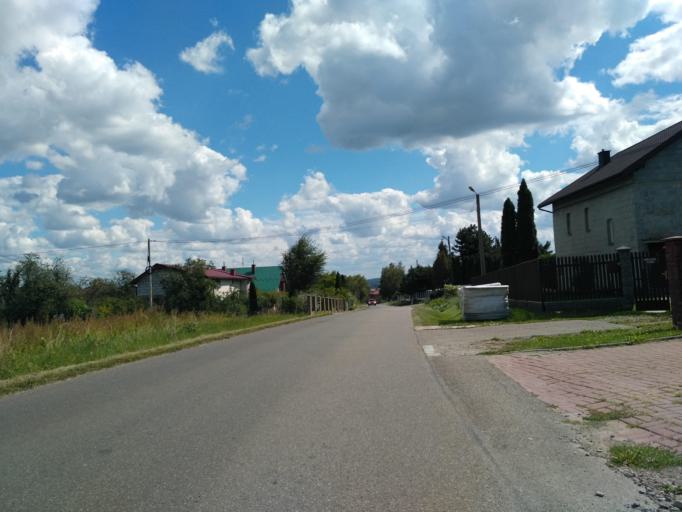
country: PL
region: Subcarpathian Voivodeship
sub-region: Powiat jasielski
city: Trzcinica
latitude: 49.7506
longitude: 21.4302
